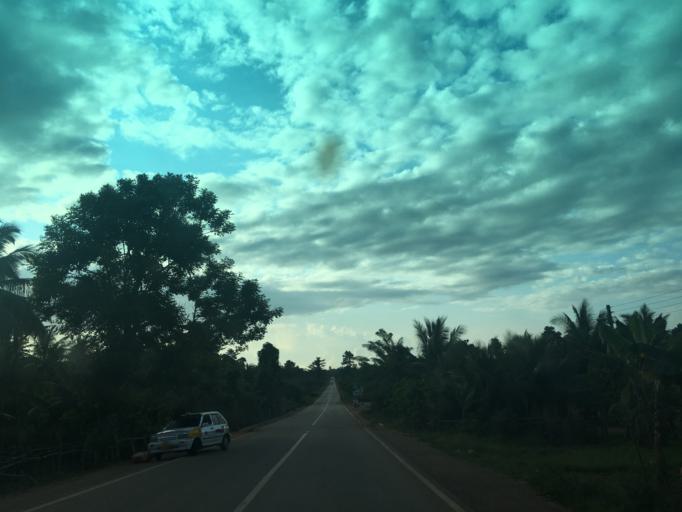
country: GH
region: Western
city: Bibiani
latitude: 6.3565
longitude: -2.2824
